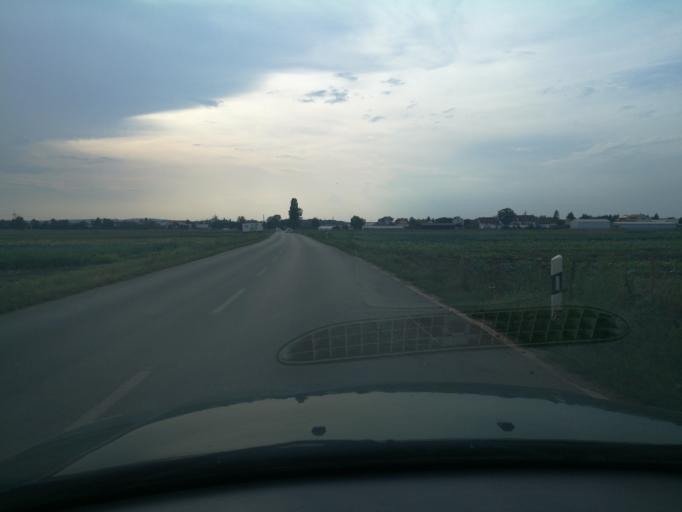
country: DE
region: Bavaria
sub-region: Regierungsbezirk Mittelfranken
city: Wetzendorf
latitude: 49.4990
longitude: 11.0280
